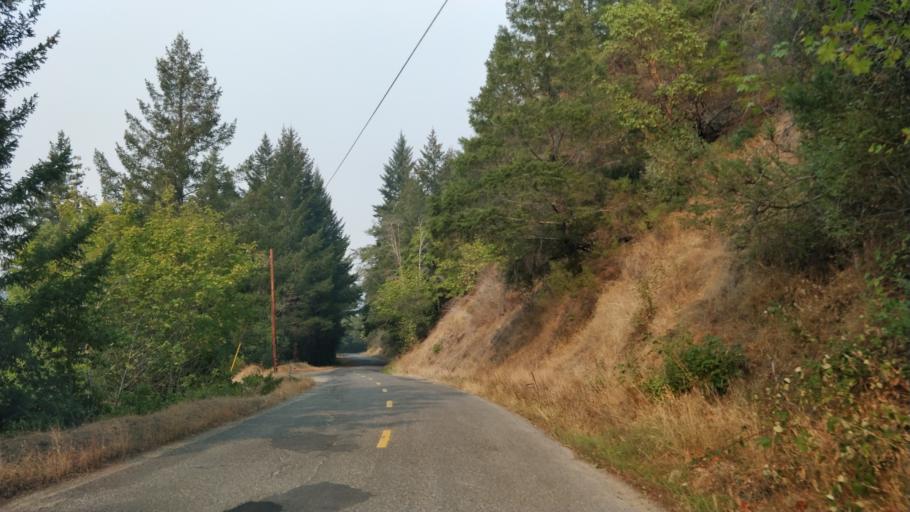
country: US
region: California
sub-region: Humboldt County
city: Rio Dell
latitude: 40.2338
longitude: -124.1369
